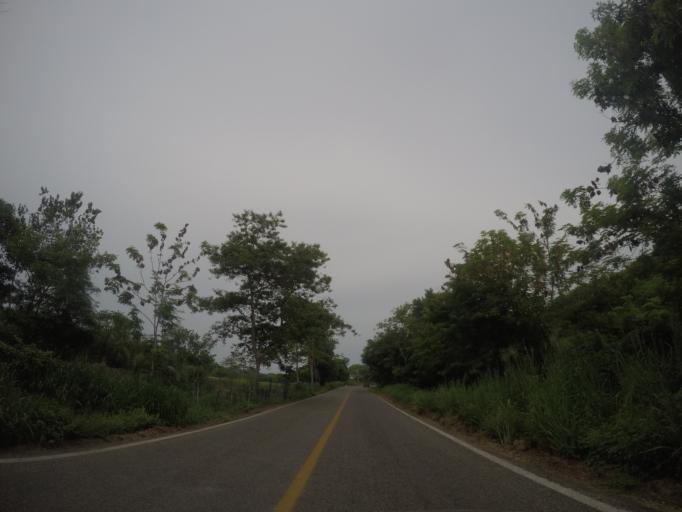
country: MX
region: Oaxaca
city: San Pedro Mixtepec
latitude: 15.9552
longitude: -97.2074
